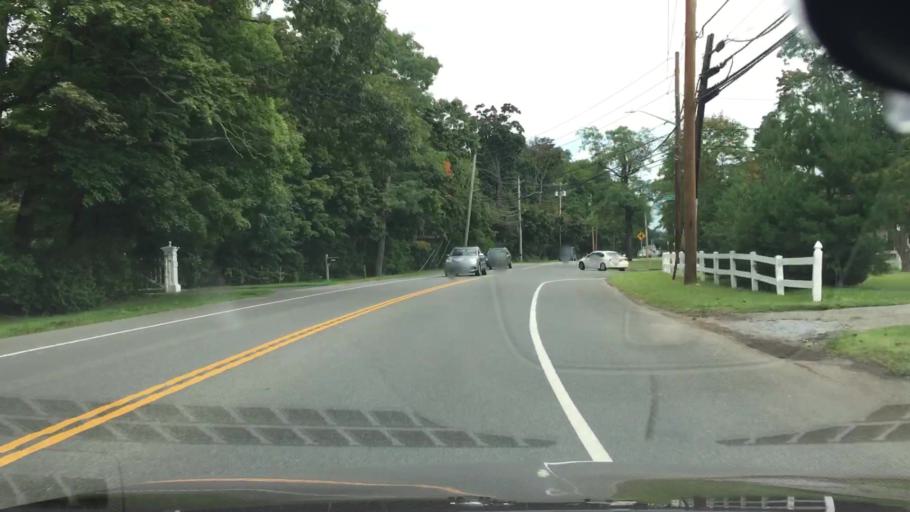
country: US
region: New York
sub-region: Suffolk County
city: Saint James
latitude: 40.8834
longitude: -73.1655
